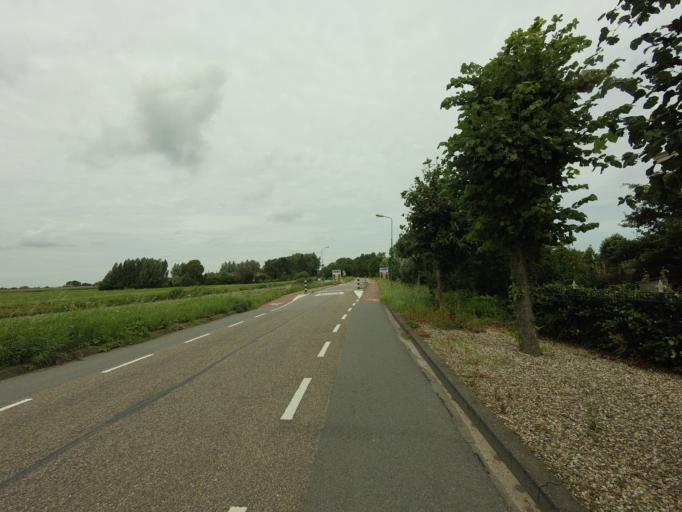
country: NL
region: Utrecht
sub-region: Stichtse Vecht
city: Vreeland
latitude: 52.2511
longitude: 4.9939
